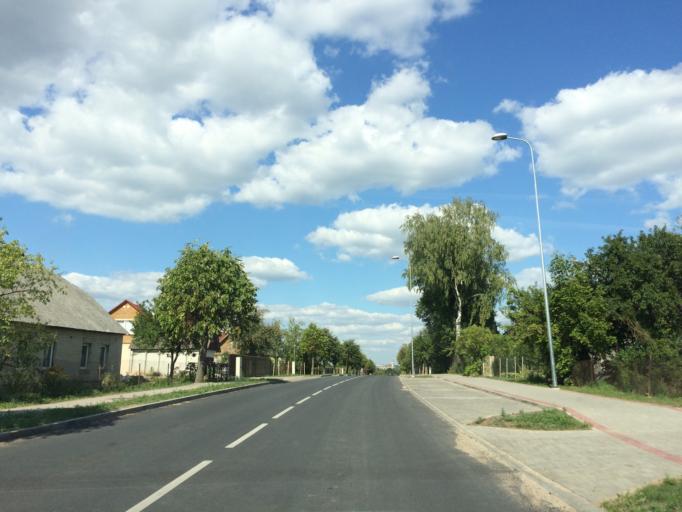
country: LV
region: Rezekne
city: Rezekne
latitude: 56.5104
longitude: 27.3422
